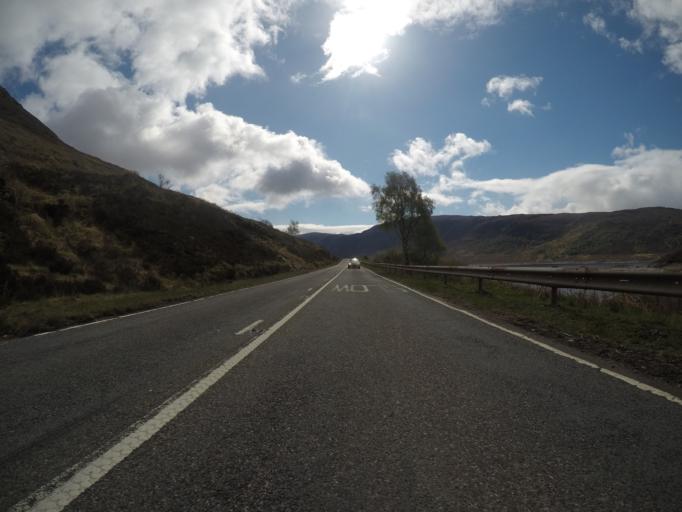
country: GB
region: Scotland
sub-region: Highland
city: Spean Bridge
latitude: 57.1503
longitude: -5.1215
